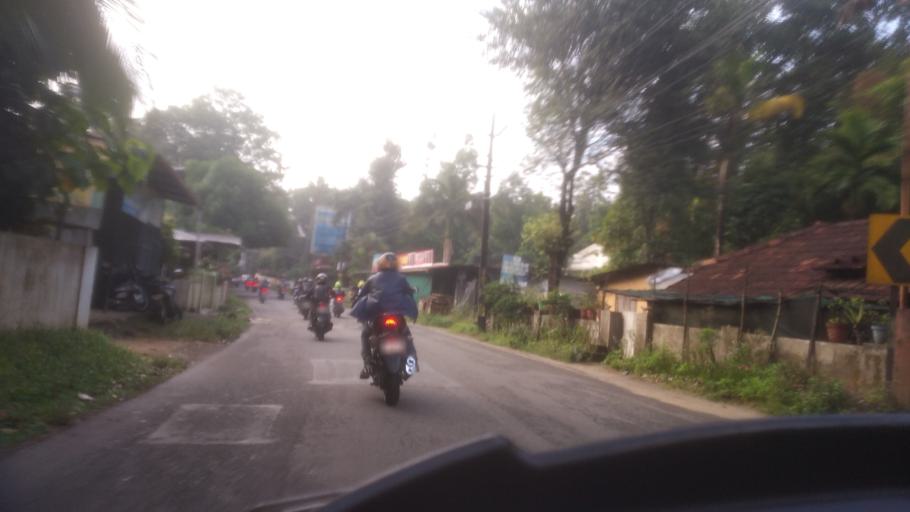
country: IN
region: Kerala
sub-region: Ernakulam
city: Perumpavur
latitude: 10.1069
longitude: 76.5361
